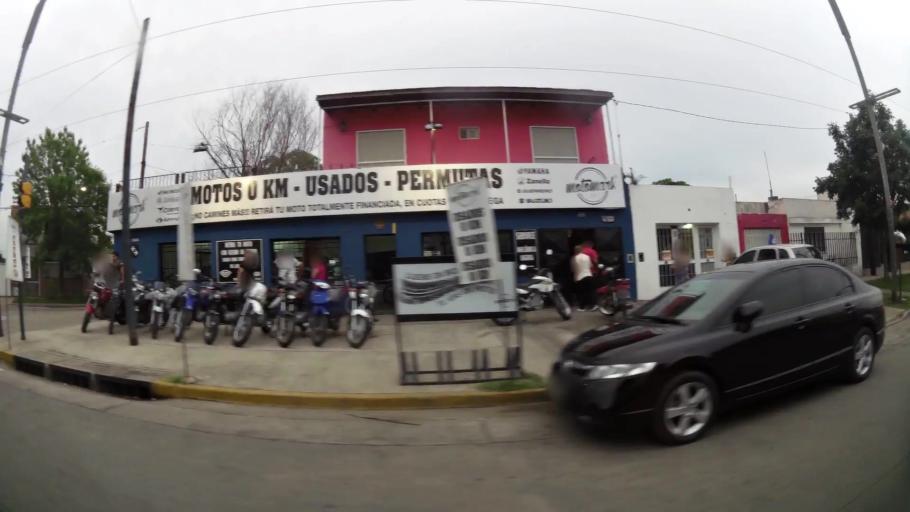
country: AR
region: Santa Fe
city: Granadero Baigorria
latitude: -32.9013
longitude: -60.7050
